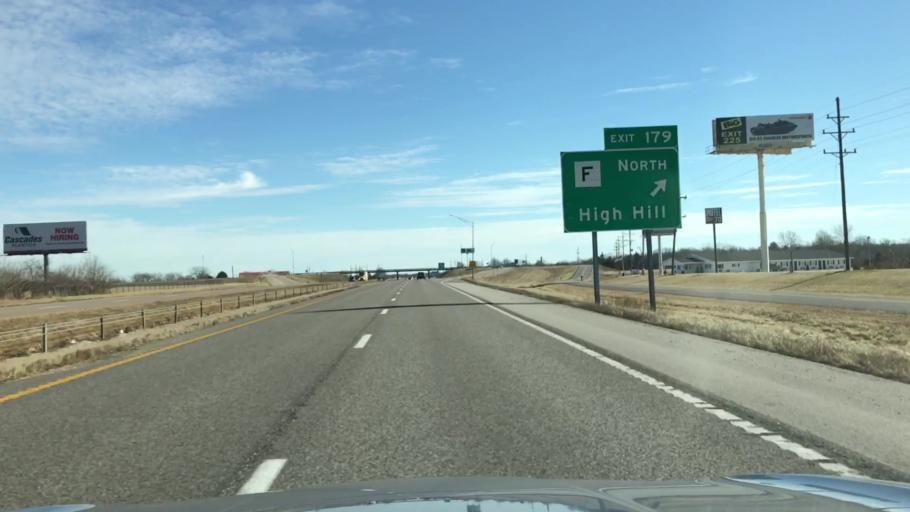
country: US
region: Missouri
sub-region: Montgomery County
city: Montgomery City
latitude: 38.8755
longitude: -91.3782
